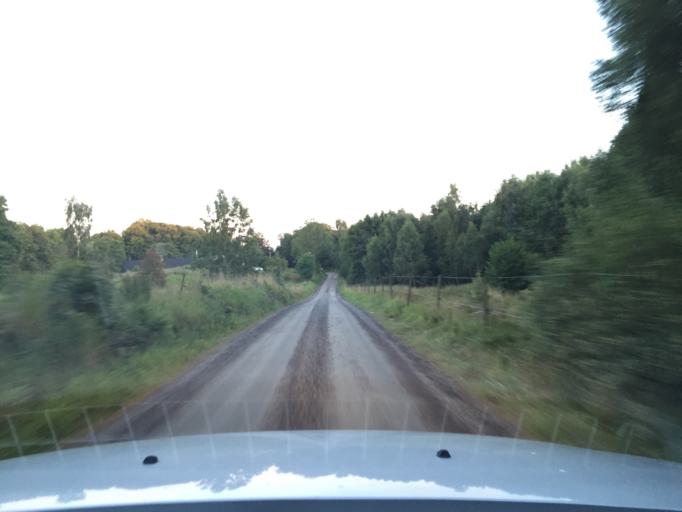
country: SE
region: Skane
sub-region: Hassleholms Kommun
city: Sosdala
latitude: 55.9987
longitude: 13.6666
